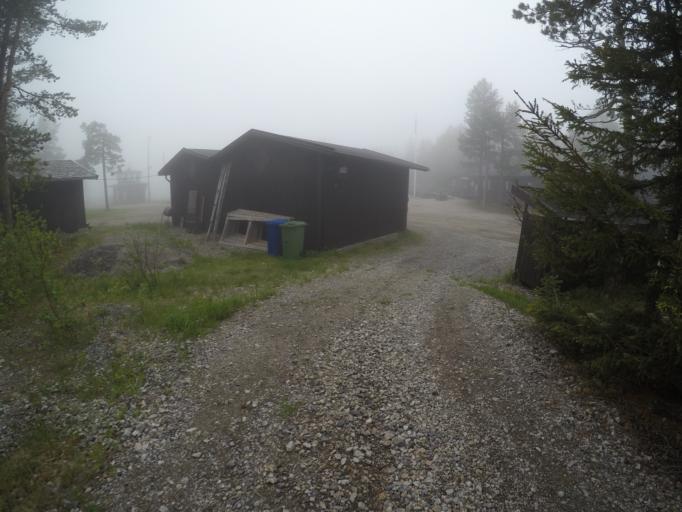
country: SE
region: Vaesternorrland
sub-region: Sundsvalls Kommun
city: Sundsvall
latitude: 62.3662
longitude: 17.3097
